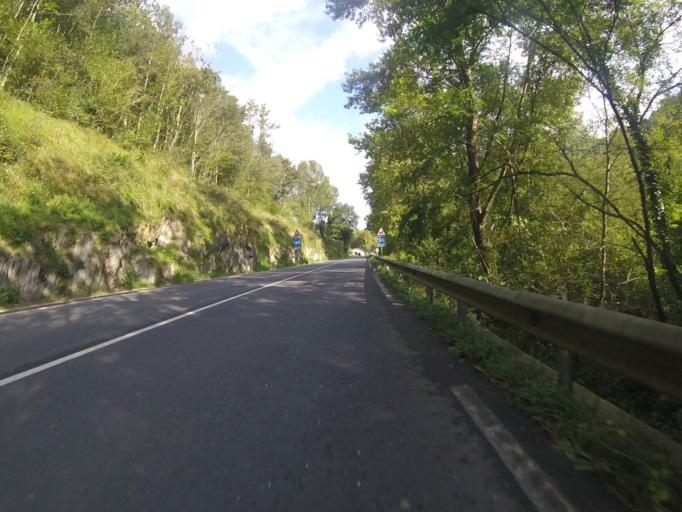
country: ES
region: Basque Country
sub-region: Provincia de Guipuzcoa
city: Amezqueta
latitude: 43.0737
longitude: -2.0869
